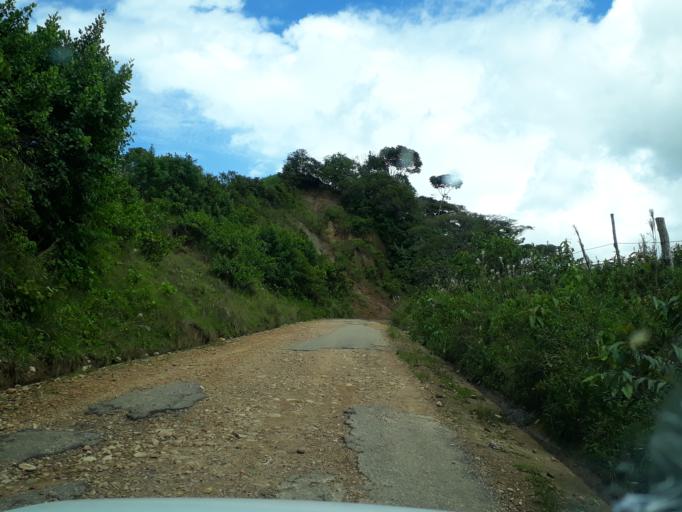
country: CO
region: Cundinamarca
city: Medina
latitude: 4.5955
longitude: -73.3044
